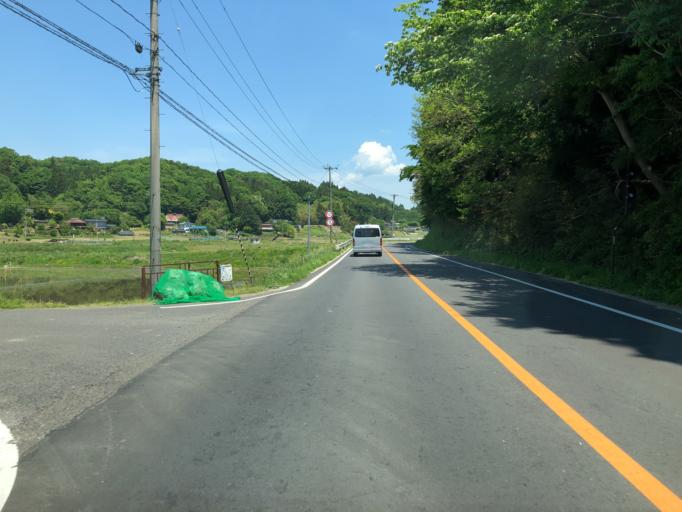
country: JP
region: Fukushima
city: Funehikimachi-funehiki
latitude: 37.4993
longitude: 140.5934
